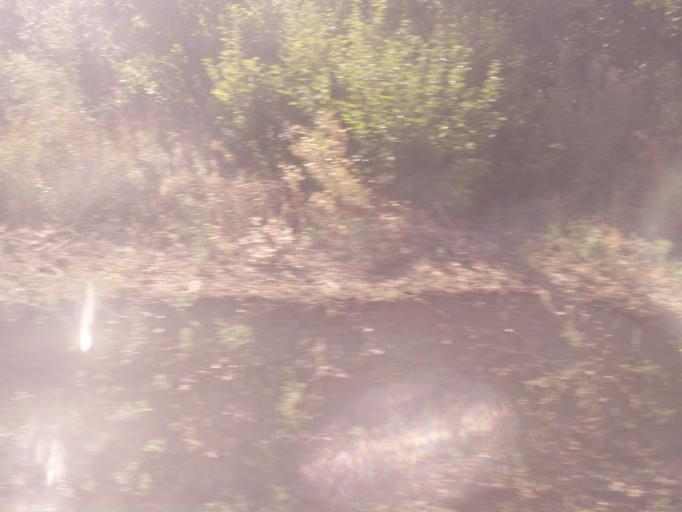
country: RU
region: Rostov
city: Krasnyy Sulin
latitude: 47.8758
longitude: 40.1256
